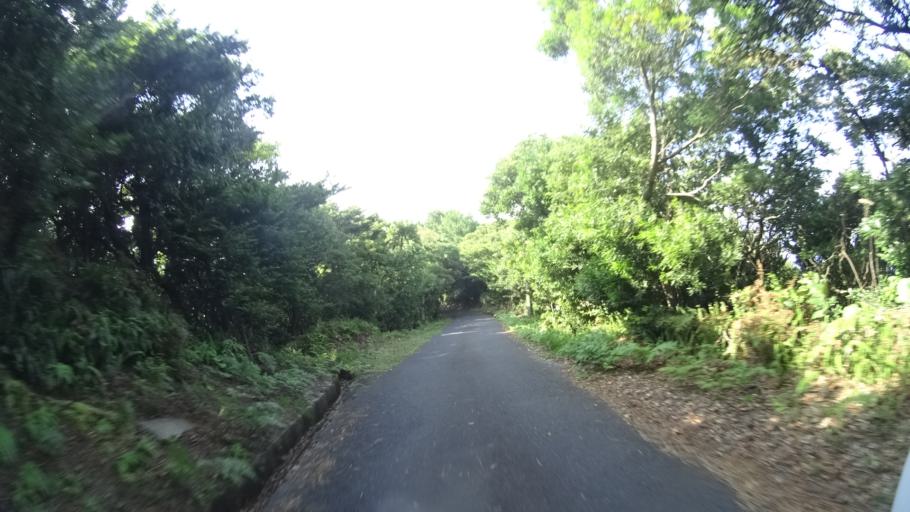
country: JP
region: Kagoshima
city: Nishinoomote
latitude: 30.3909
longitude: 130.3834
